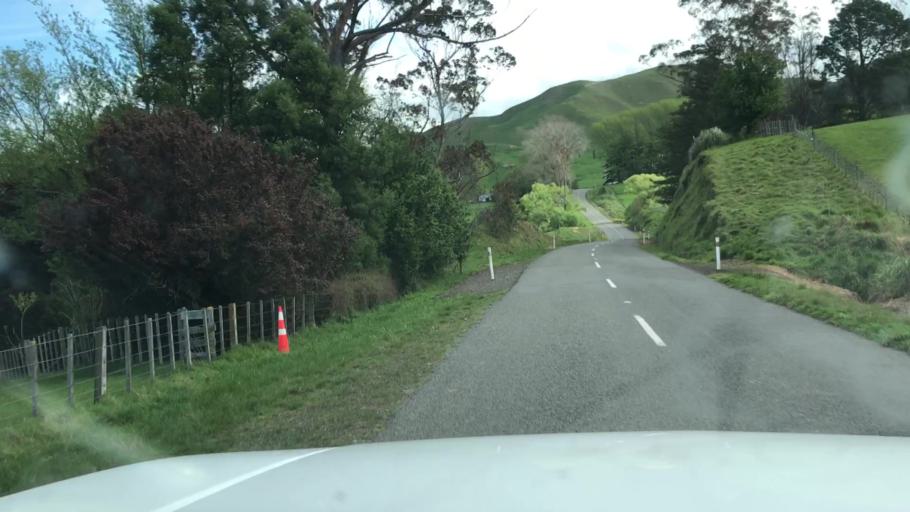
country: NZ
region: Hawke's Bay
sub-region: Hastings District
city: Hastings
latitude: -39.8189
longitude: 176.7417
